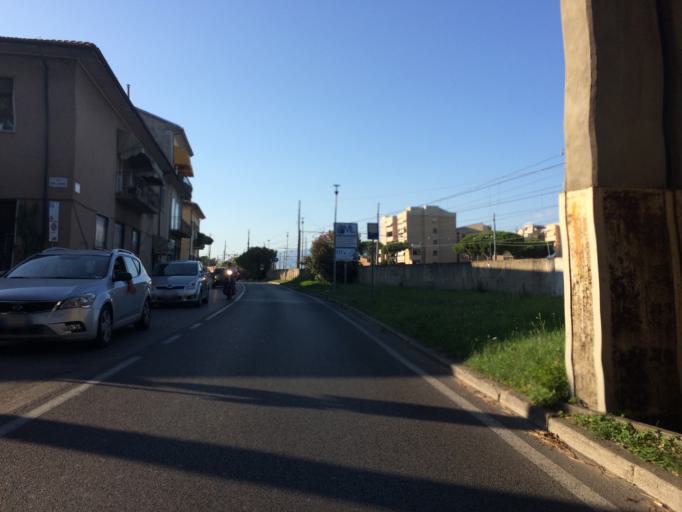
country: IT
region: Tuscany
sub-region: Provincia di Lucca
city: Viareggio
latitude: 43.8675
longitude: 10.2564
